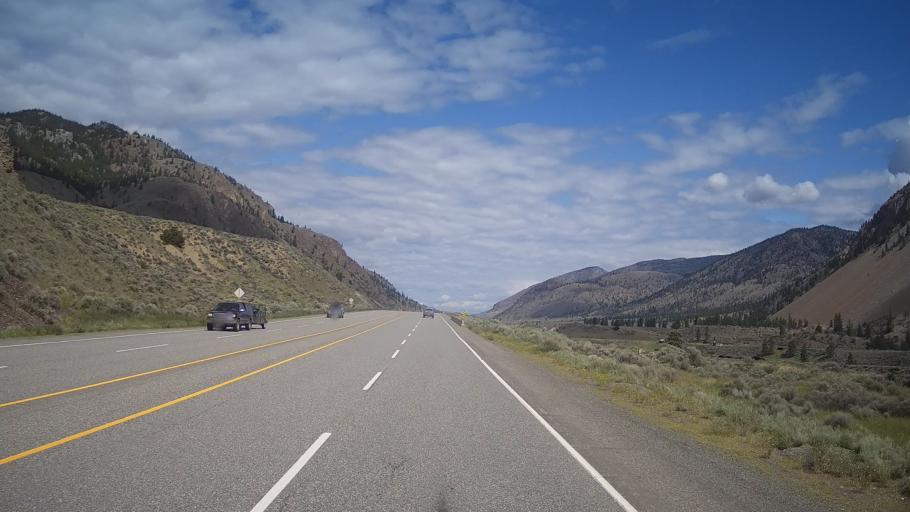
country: CA
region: British Columbia
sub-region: Thompson-Nicola Regional District
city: Ashcroft
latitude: 50.5133
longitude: -121.2811
